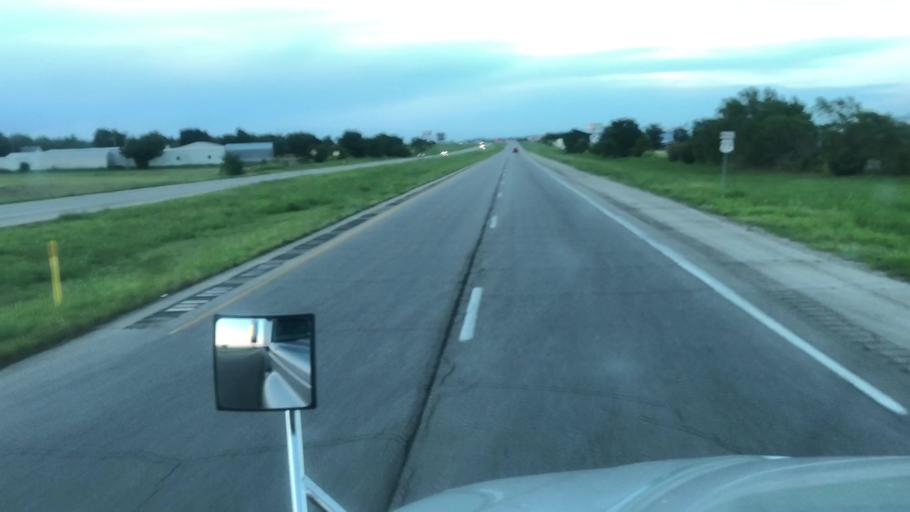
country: US
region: Oklahoma
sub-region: Kay County
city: Ponca City
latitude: 36.7531
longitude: -97.0659
